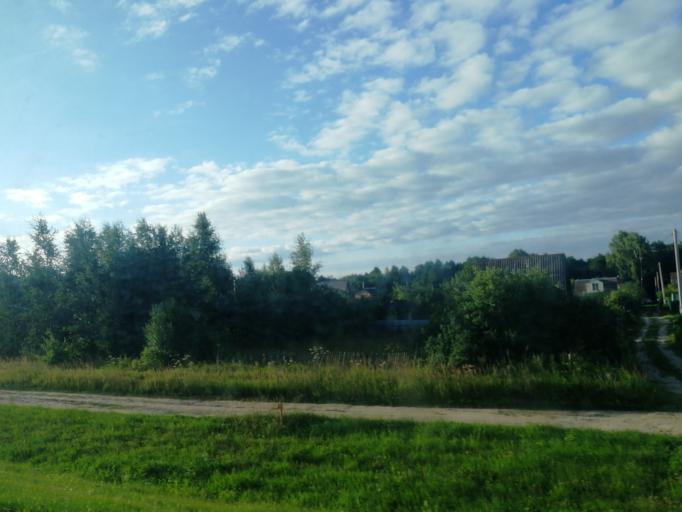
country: RU
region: Kaluga
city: Kaluga
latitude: 54.4359
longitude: 36.3473
